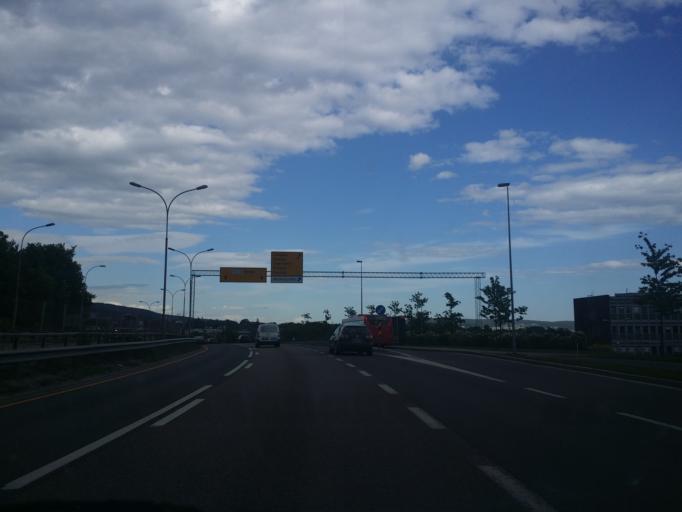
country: NO
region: Oslo
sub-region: Oslo
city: Sjolyststranda
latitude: 59.9459
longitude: 10.7149
